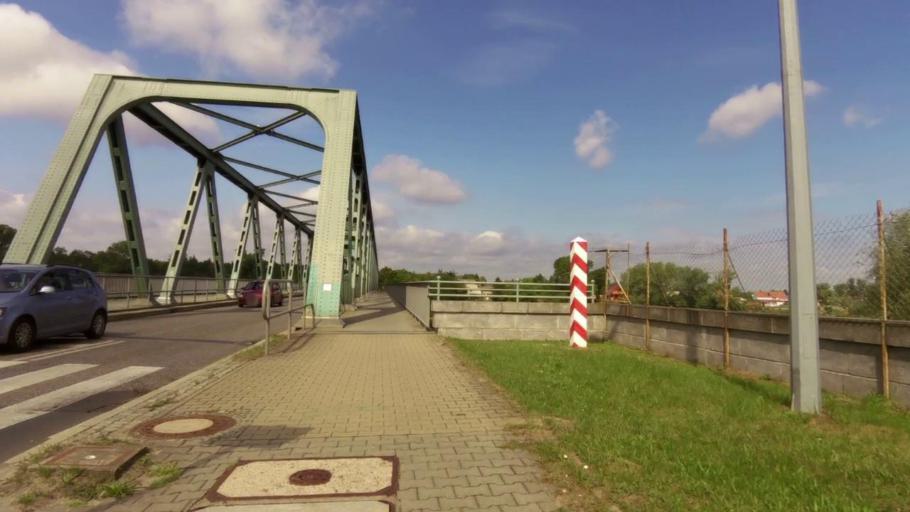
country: DE
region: Brandenburg
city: Oderberg
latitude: 52.8430
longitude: 14.1252
